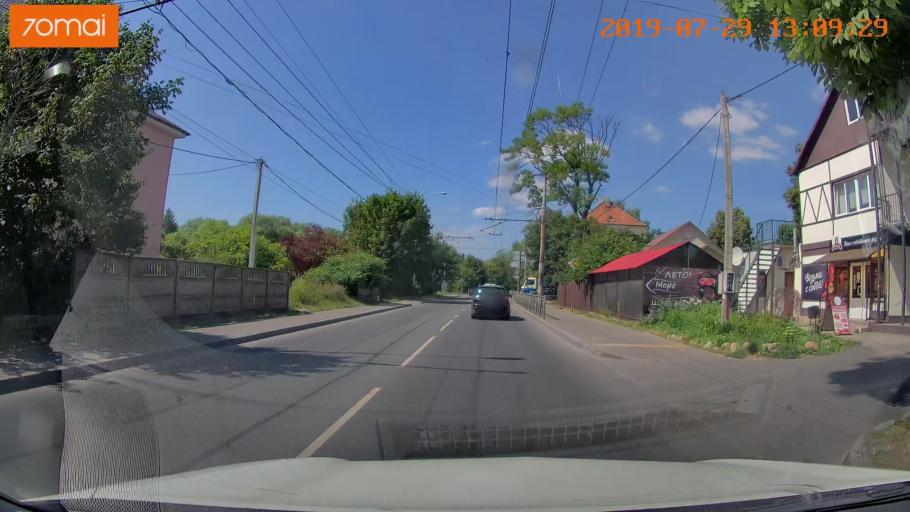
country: RU
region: Kaliningrad
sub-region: Gorod Kaliningrad
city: Kaliningrad
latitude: 54.7138
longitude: 20.4172
